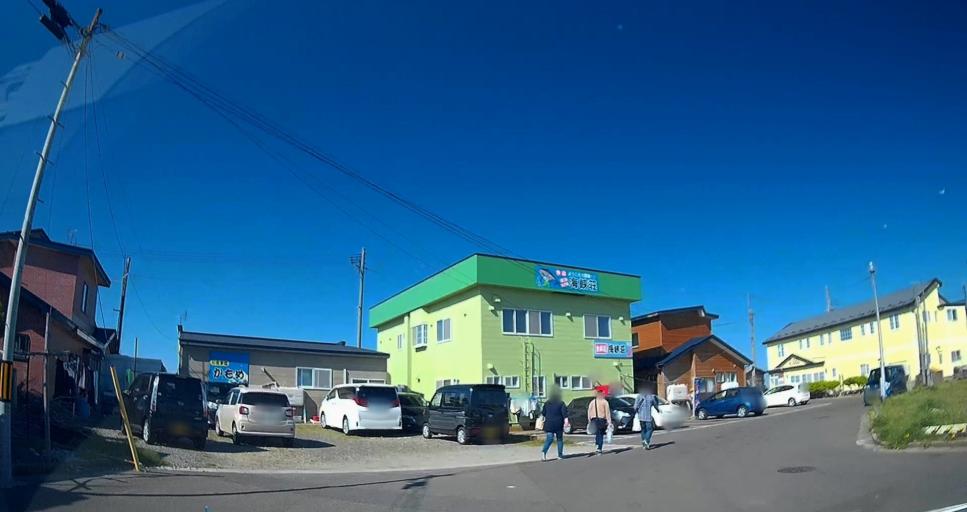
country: JP
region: Hokkaido
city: Hakodate
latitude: 41.5458
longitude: 140.9130
